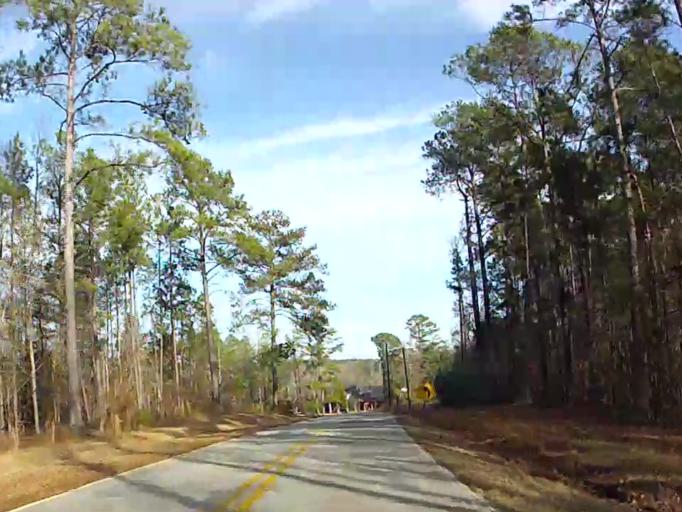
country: US
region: Georgia
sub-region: Bibb County
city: West Point
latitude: 32.9559
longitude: -83.7843
